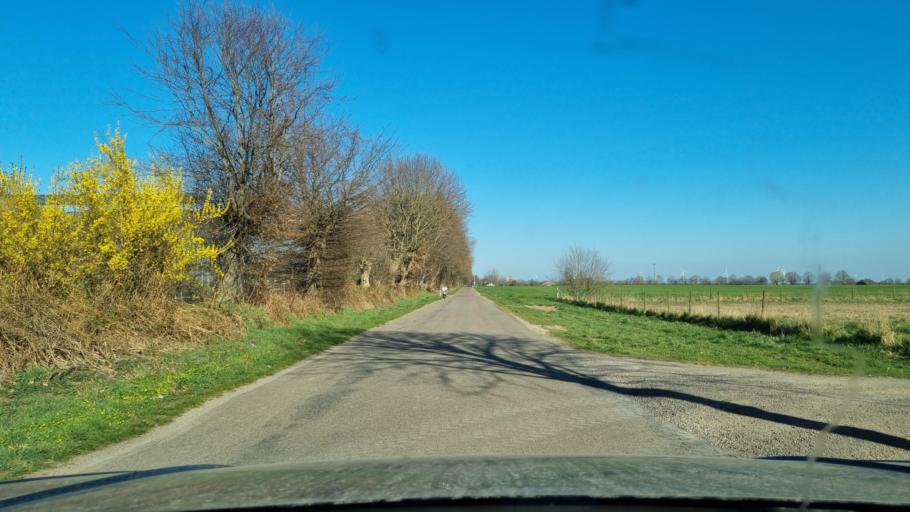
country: DE
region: North Rhine-Westphalia
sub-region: Regierungsbezirk Dusseldorf
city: Goch
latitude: 51.7155
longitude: 6.1316
